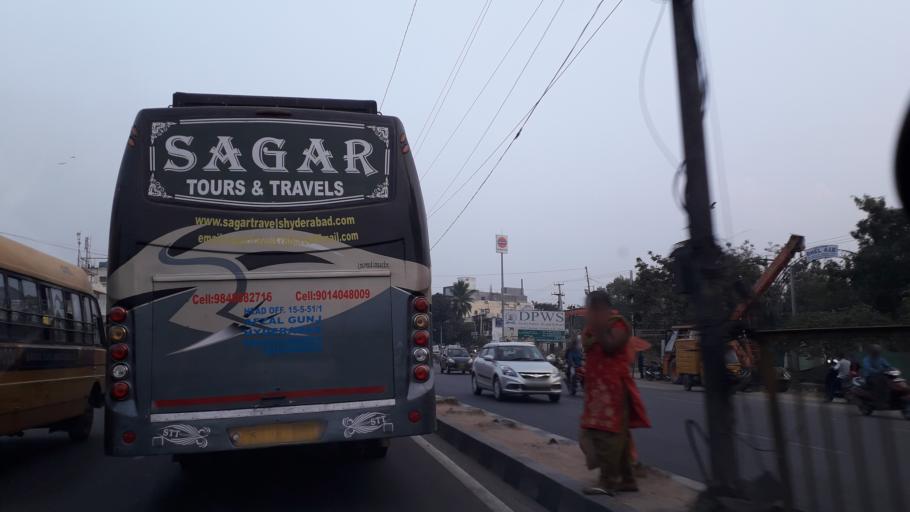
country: IN
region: Telangana
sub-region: Medak
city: Serilingampalle
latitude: 17.5050
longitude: 78.3075
